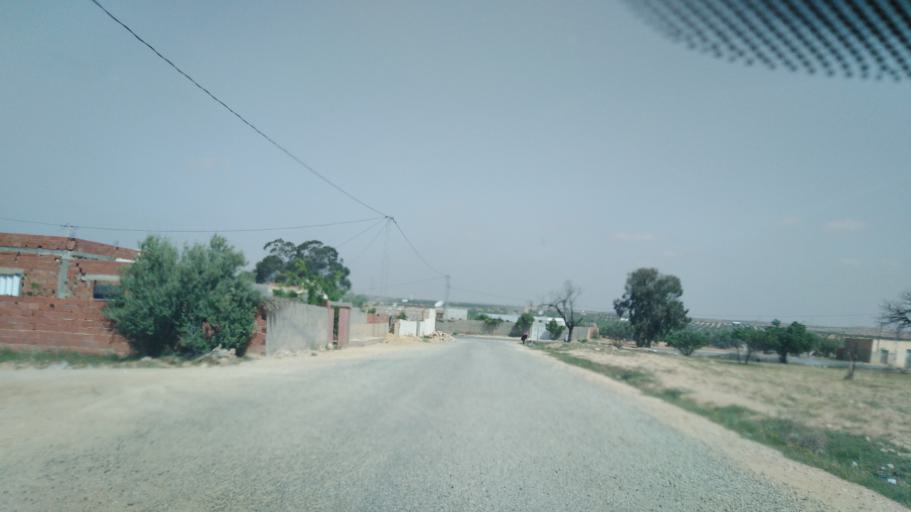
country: TN
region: Safaqis
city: Sfax
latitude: 34.7293
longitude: 10.5720
